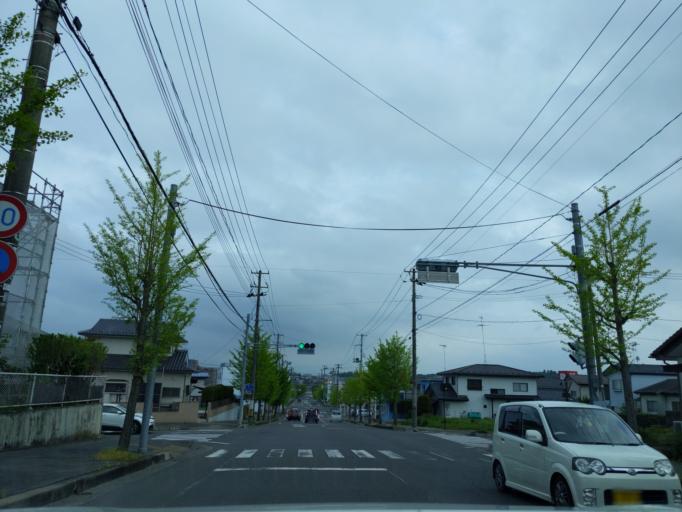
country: JP
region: Fukushima
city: Sukagawa
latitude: 37.2987
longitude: 140.3610
